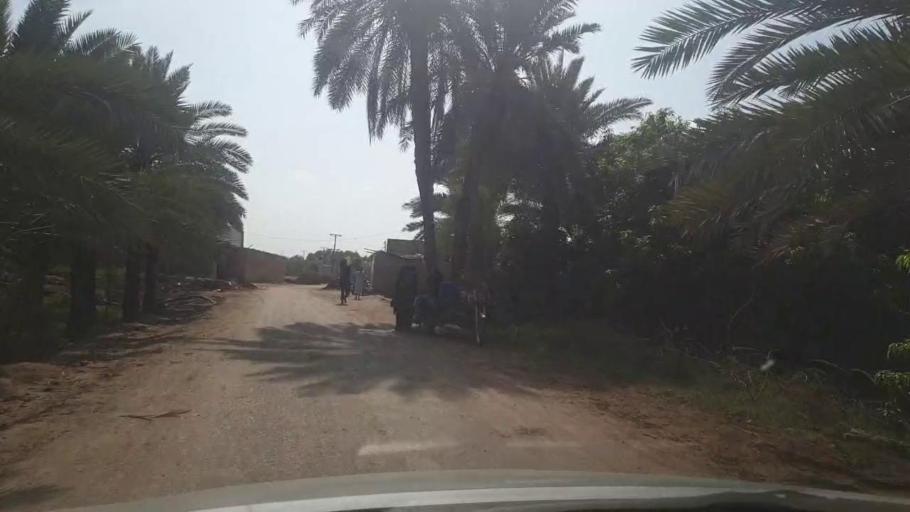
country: PK
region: Sindh
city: Khairpur
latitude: 27.5379
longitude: 68.7681
